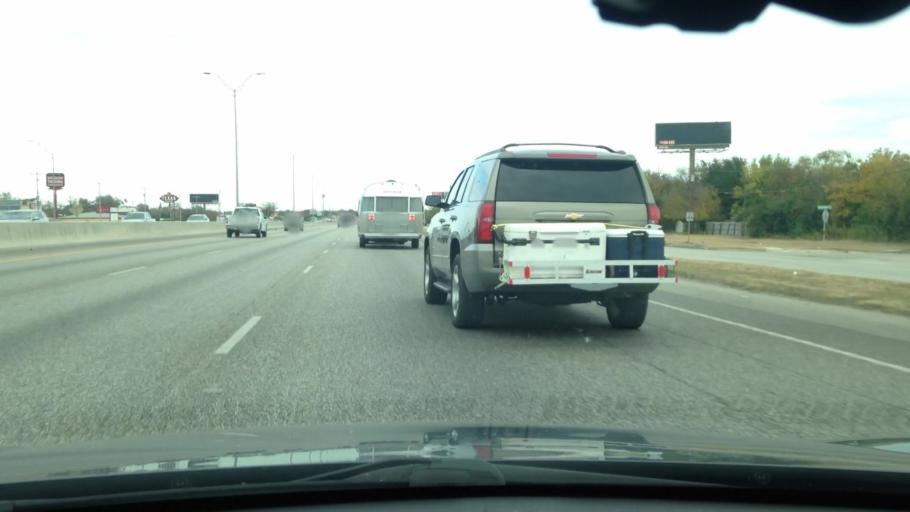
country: US
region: Texas
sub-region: Hays County
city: San Marcos
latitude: 29.8628
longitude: -97.9464
